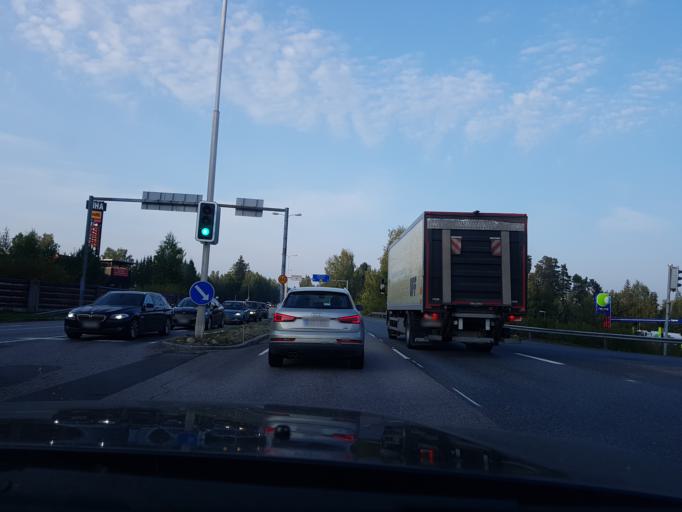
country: FI
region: Uusimaa
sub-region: Helsinki
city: Tuusula
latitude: 60.3730
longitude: 25.0180
